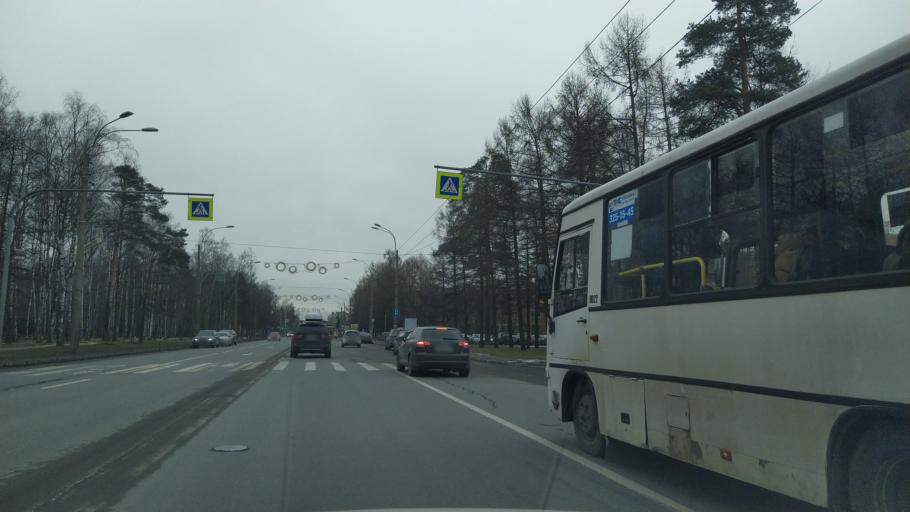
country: RU
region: St.-Petersburg
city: Sosnovka
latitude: 60.0150
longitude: 30.3403
